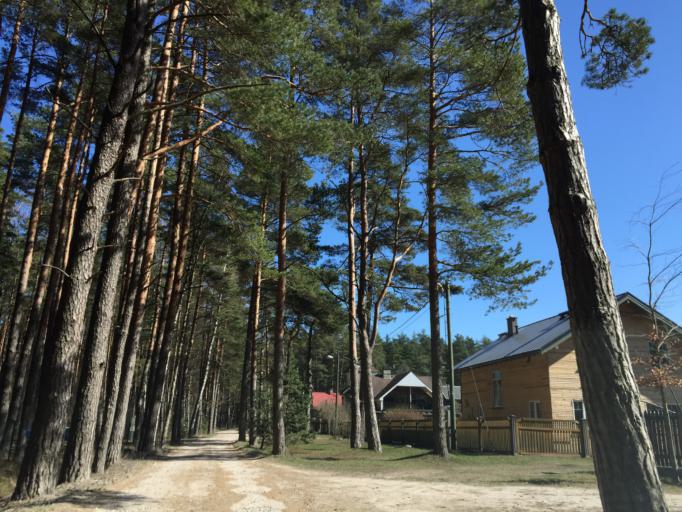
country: LV
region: Jurmala
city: Jurmala
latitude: 56.9493
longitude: 23.6821
